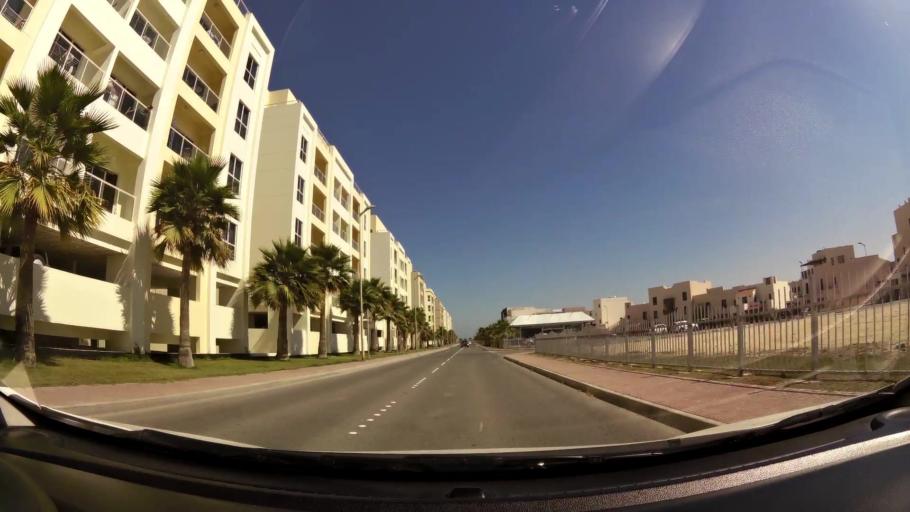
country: BH
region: Muharraq
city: Al Hadd
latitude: 26.2872
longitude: 50.6685
